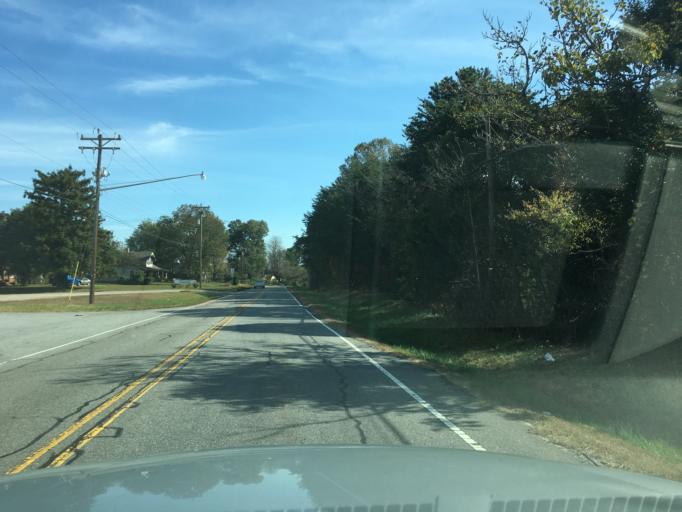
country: US
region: North Carolina
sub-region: Catawba County
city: Saint Stephens
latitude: 35.7320
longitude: -81.2885
